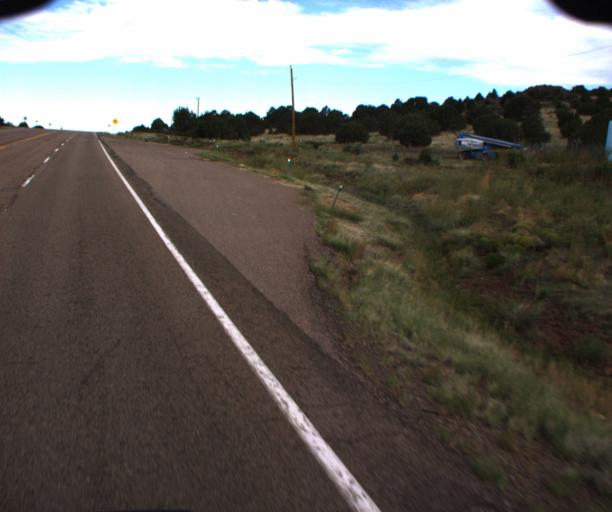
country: US
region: Arizona
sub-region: Apache County
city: Springerville
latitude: 34.2656
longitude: -109.5779
